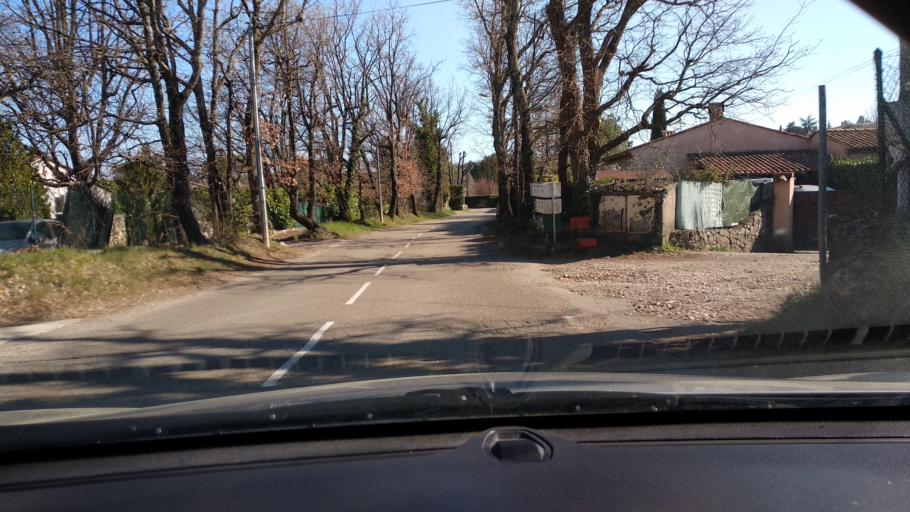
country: FR
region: Provence-Alpes-Cote d'Azur
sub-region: Departement des Alpes-Maritimes
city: Saint-Cezaire-sur-Siagne
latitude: 43.6550
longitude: 6.7956
